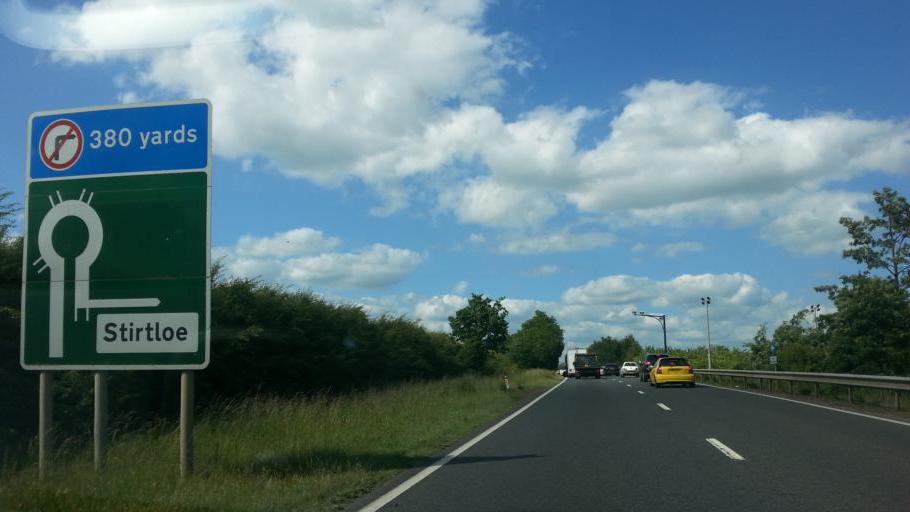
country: GB
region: England
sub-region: Cambridgeshire
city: Buckden
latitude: 52.2845
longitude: -0.2577
